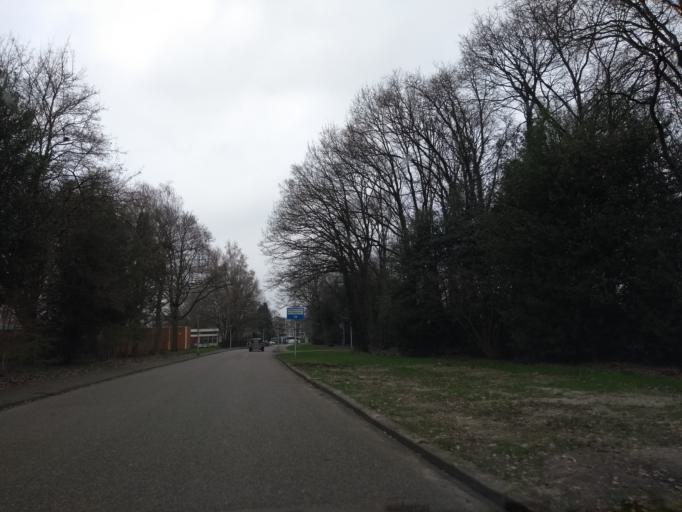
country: NL
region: Overijssel
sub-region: Gemeente Enschede
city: Enschede
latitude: 52.1920
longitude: 6.8748
